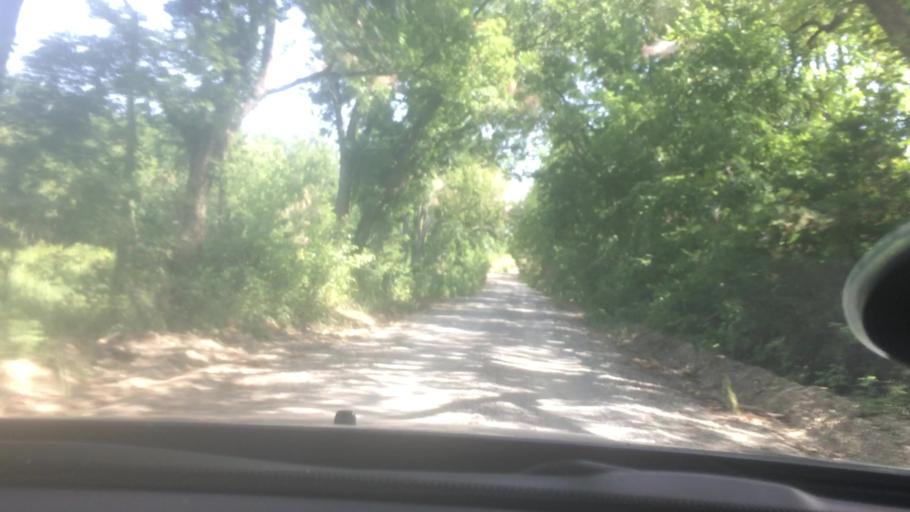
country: US
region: Oklahoma
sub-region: Bryan County
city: Durant
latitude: 34.0988
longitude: -96.4077
